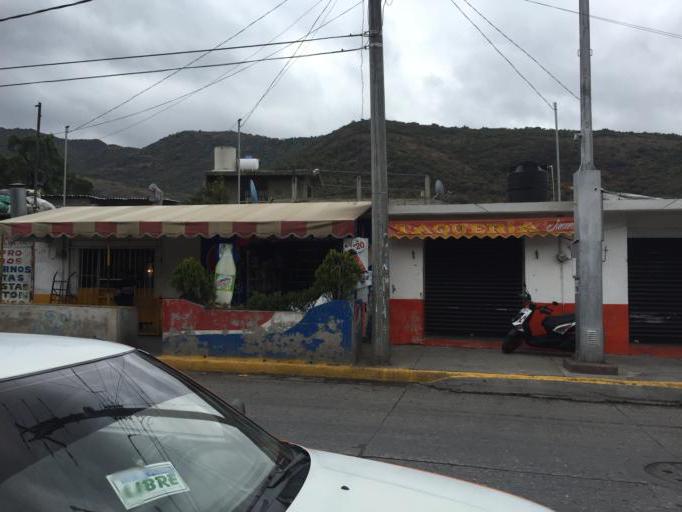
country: MX
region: Mexico
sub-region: Tlalnepantla de Baz
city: Puerto Escondido (Tepeolulco Puerto Escondido)
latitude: 19.5652
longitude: -99.0873
